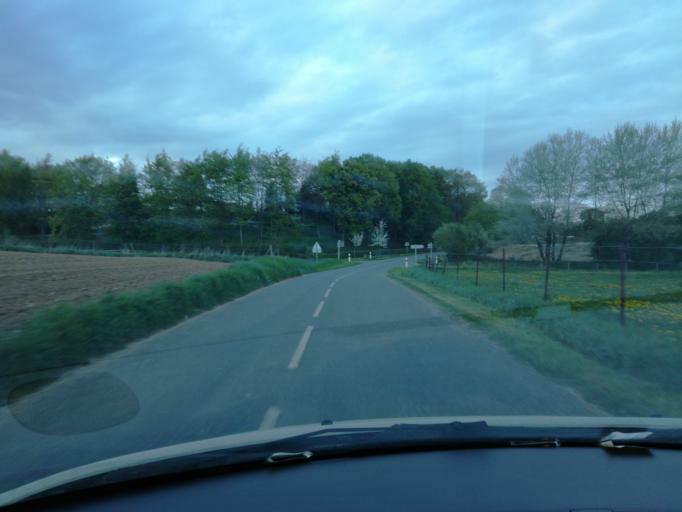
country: FR
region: Picardie
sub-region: Departement de la Somme
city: Poix-de-Picardie
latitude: 49.8174
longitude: 2.0174
